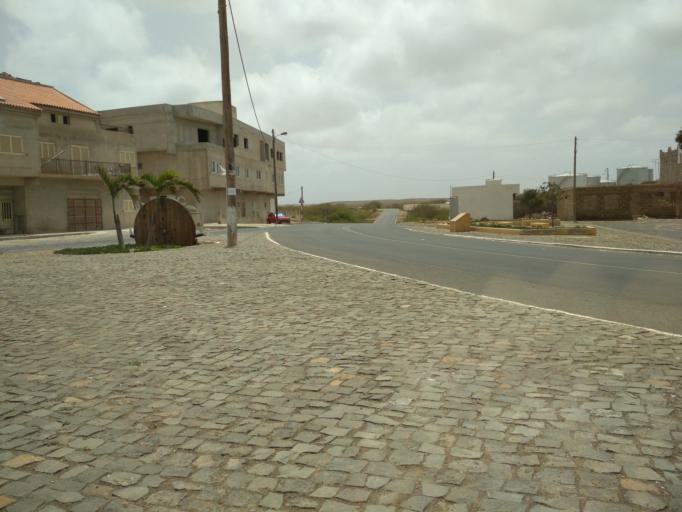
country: CV
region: Sal
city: Espargos
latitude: 16.7589
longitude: -22.9801
